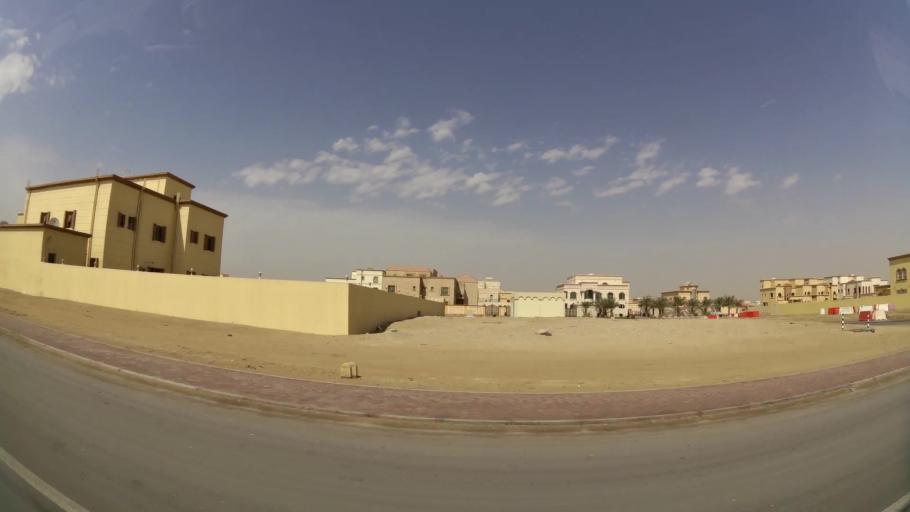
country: AE
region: Abu Dhabi
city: Abu Dhabi
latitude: 24.3156
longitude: 54.5437
